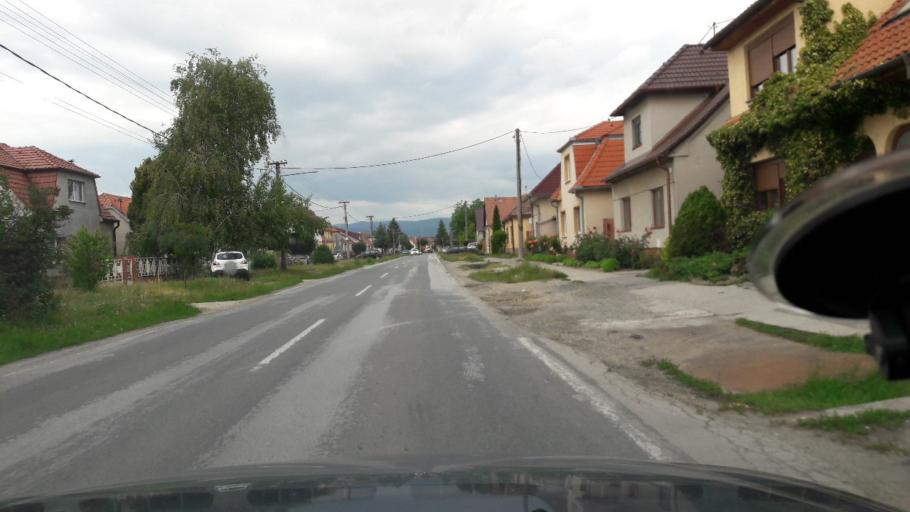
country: SK
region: Bratislavsky
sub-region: Okres Pezinok
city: Pezinok
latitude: 48.2739
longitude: 17.3000
